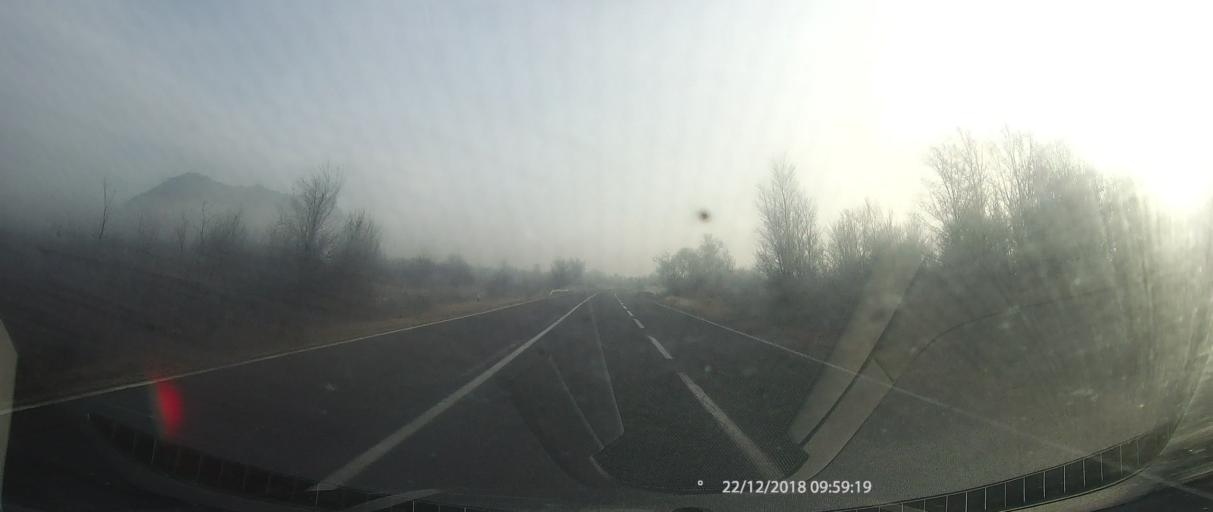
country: MK
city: Klechovce
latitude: 42.1516
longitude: 21.9565
